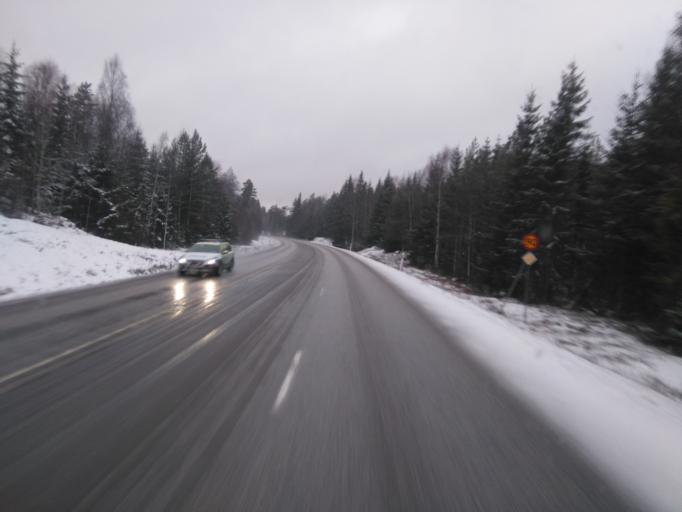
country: SE
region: Joenkoeping
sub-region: Eksjo Kommun
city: Eksjoe
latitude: 57.6484
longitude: 15.0547
